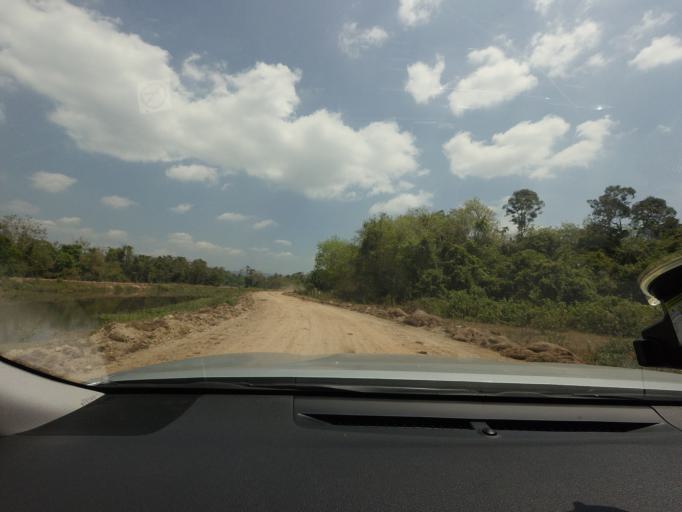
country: TH
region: Narathiwat
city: Rueso
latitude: 6.3891
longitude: 101.4994
